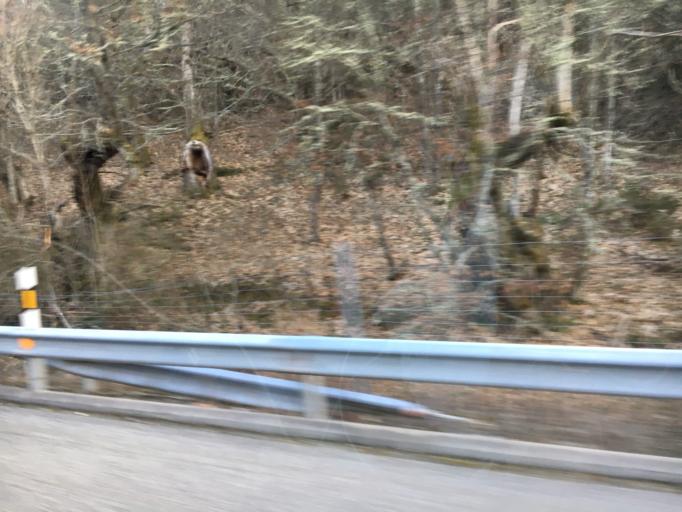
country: ES
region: Castille and Leon
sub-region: Provincia de Leon
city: Trabadelo
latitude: 42.6465
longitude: -6.8809
